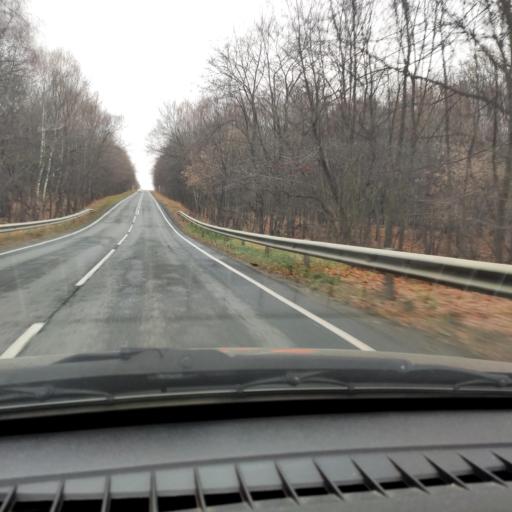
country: RU
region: Samara
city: Zhigulevsk
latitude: 53.3392
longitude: 49.4992
